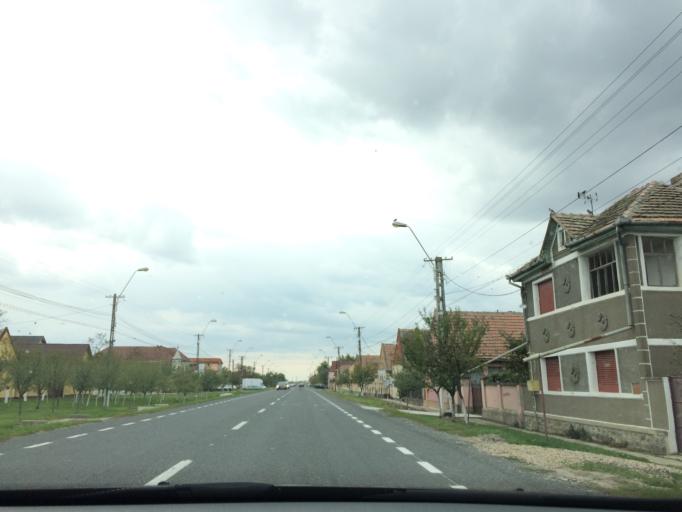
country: RO
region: Timis
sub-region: Oras Recas
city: Izvin
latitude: 45.7983
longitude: 21.4544
